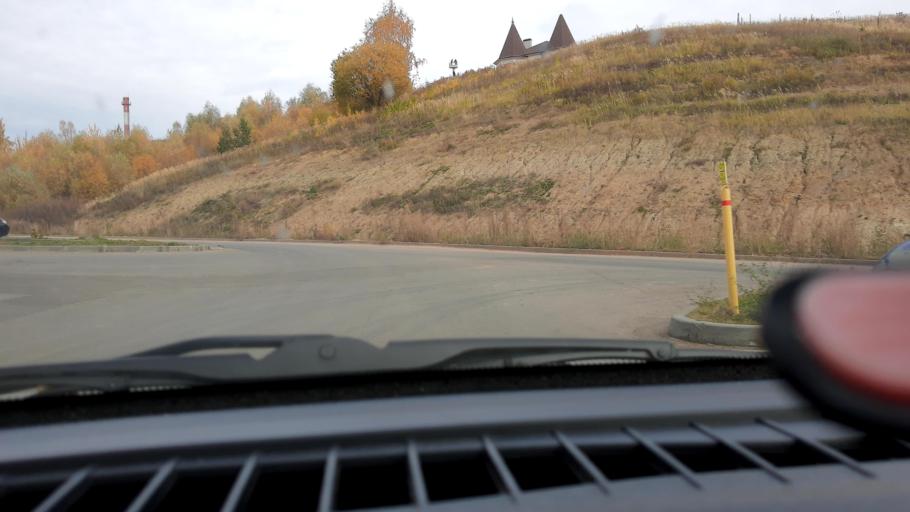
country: RU
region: Nizjnij Novgorod
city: Afonino
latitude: 56.2802
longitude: 44.0910
